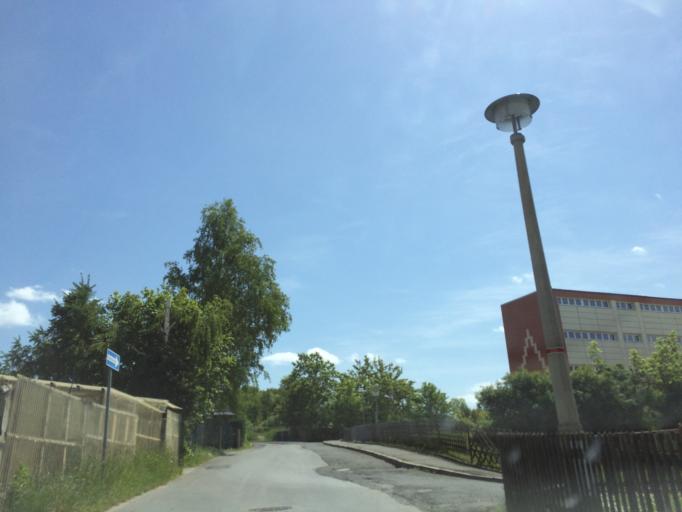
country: DE
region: Thuringia
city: Ranis
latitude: 50.6602
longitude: 11.5712
